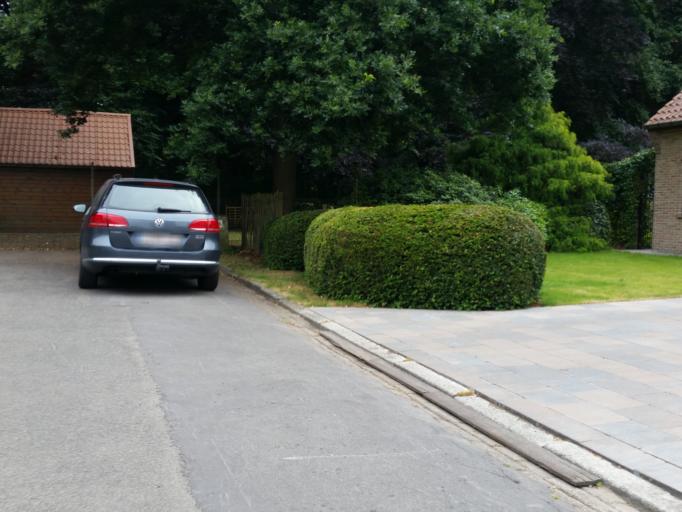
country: BE
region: Flanders
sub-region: Provincie Antwerpen
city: Mechelen
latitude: 51.0486
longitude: 4.4727
